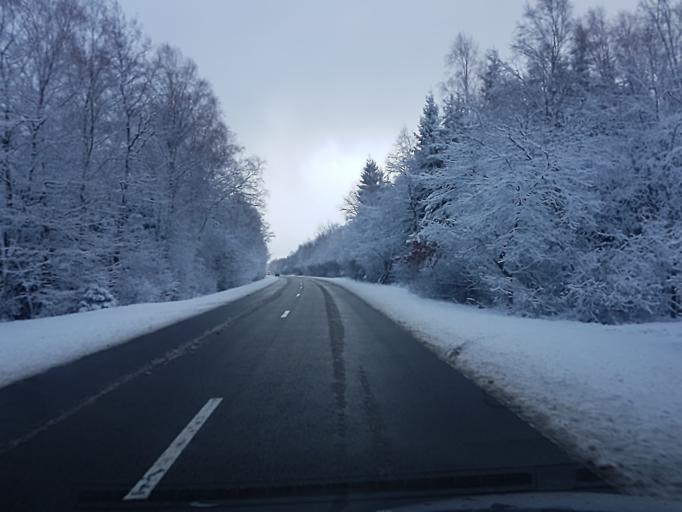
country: BE
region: Wallonia
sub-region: Province de Liege
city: Jalhay
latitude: 50.5445
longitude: 6.0106
